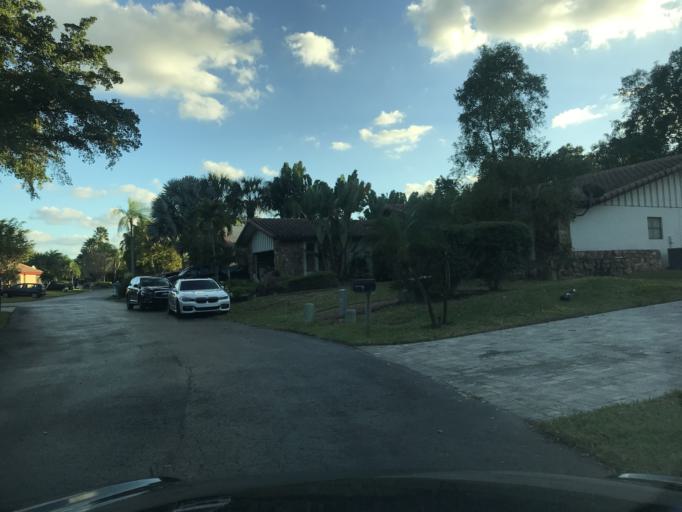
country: US
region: Florida
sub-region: Broward County
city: Pine Island Ridge
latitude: 26.1165
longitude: -80.2730
